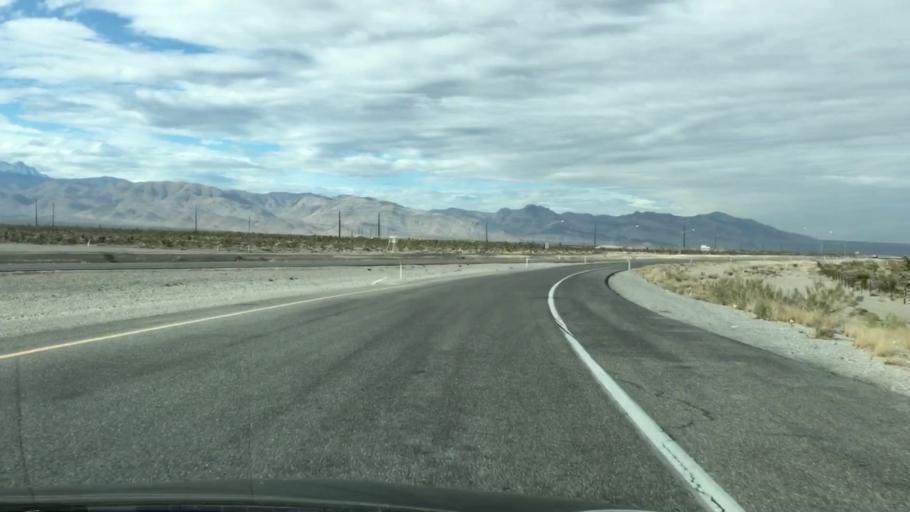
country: US
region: Nevada
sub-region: Clark County
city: Summerlin South
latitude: 36.3637
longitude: -115.3520
